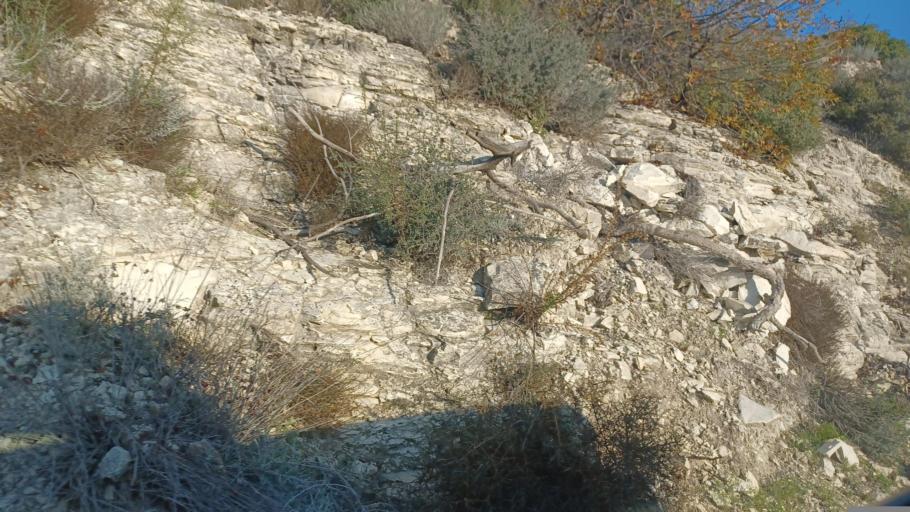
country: CY
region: Larnaka
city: Kofinou
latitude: 34.8218
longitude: 33.3122
